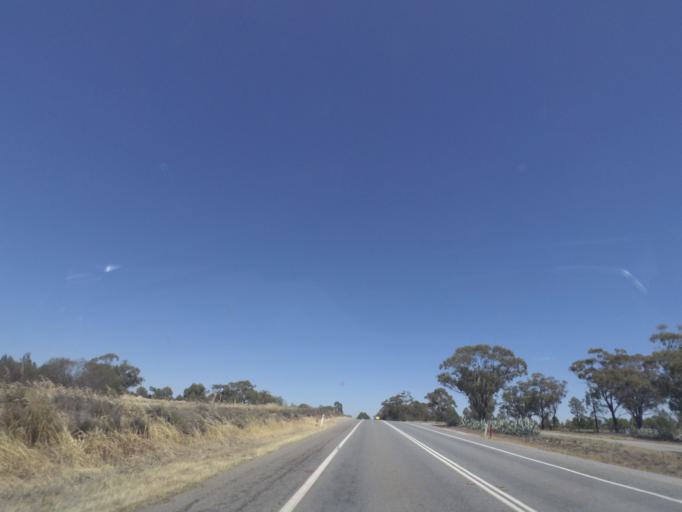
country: AU
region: New South Wales
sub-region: Narrandera
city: Narrandera
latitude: -34.7360
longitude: 146.6012
